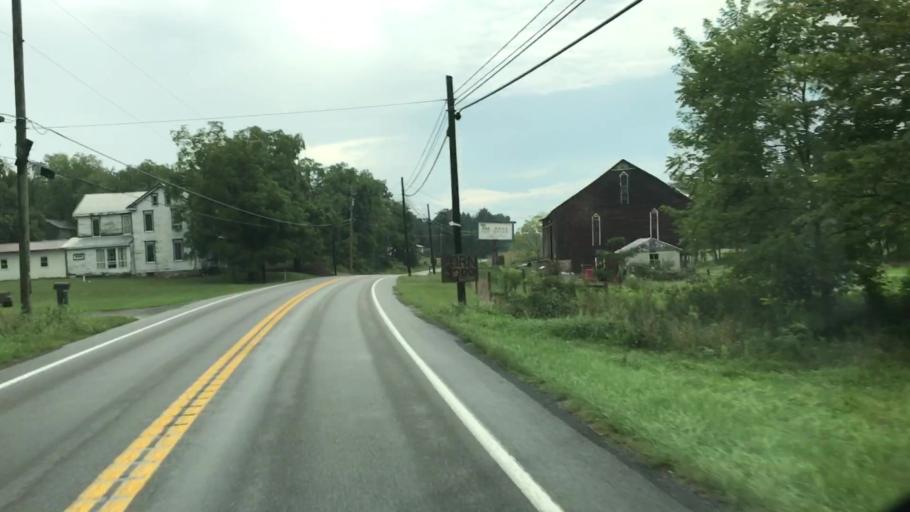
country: US
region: Pennsylvania
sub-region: Perry County
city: New Bloomfield
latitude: 40.3778
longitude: -77.1518
